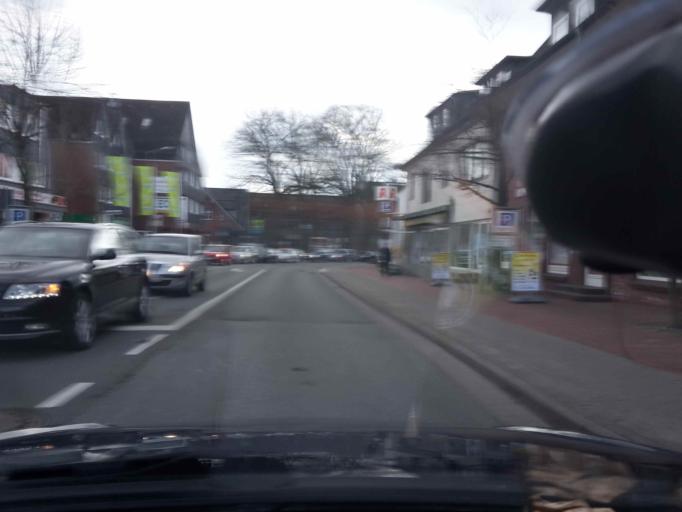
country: DE
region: Lower Saxony
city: Buchholz in der Nordheide
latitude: 53.3310
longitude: 9.8822
